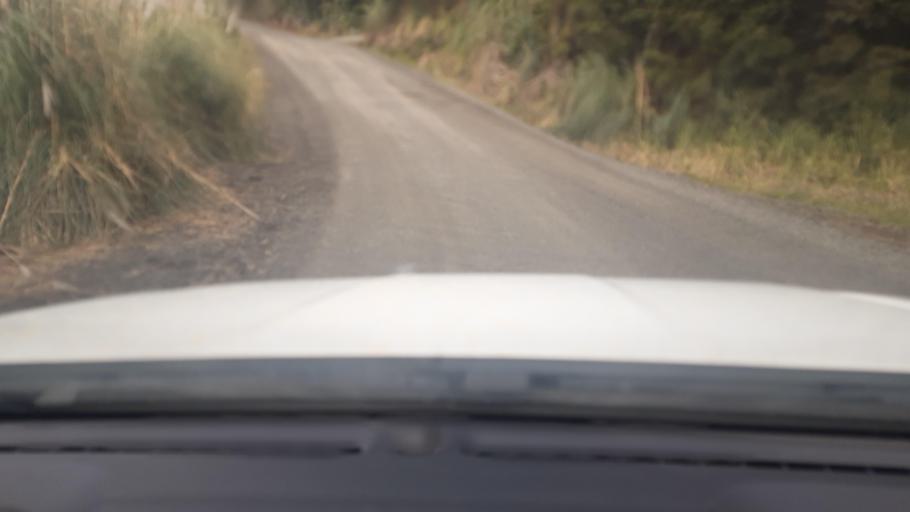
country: NZ
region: Northland
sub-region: Far North District
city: Ahipara
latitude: -35.2792
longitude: 173.2089
